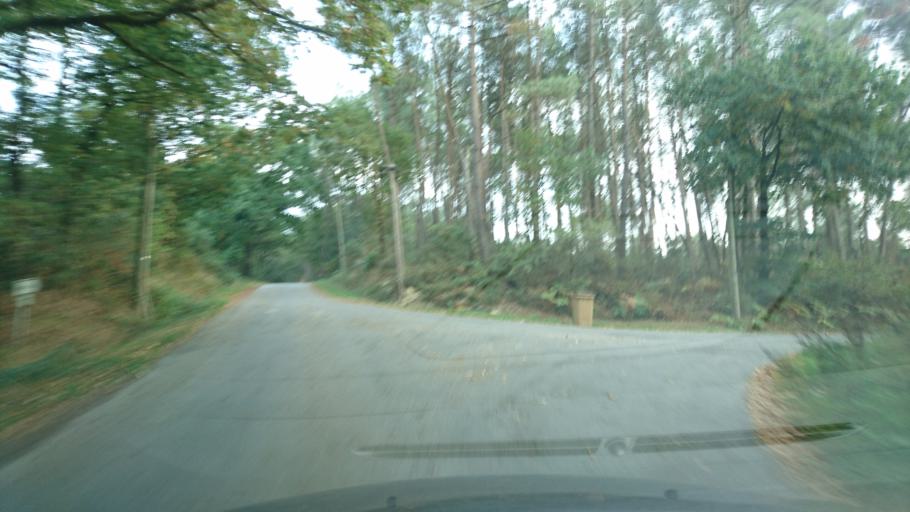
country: FR
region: Brittany
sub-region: Departement du Morbihan
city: Saint-Vincent-sur-Oust
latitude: 47.6974
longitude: -2.1323
